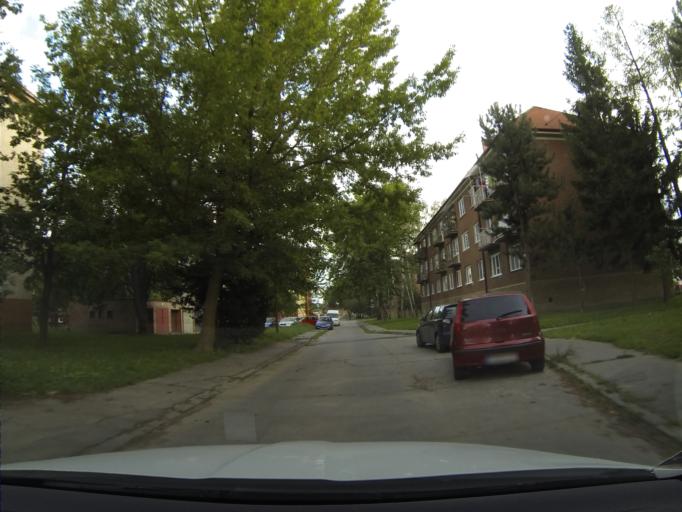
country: SK
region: Nitriansky
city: Bojnice
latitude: 48.7714
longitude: 18.5990
